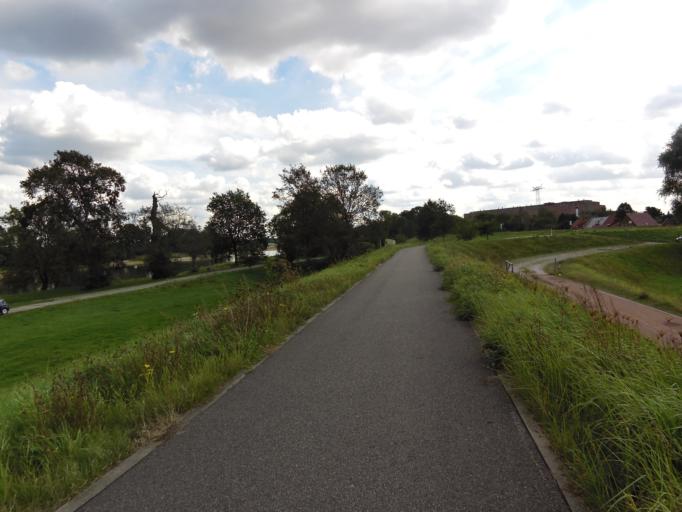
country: DE
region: Saxony-Anhalt
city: Vockerode
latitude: 51.8521
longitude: 12.3533
